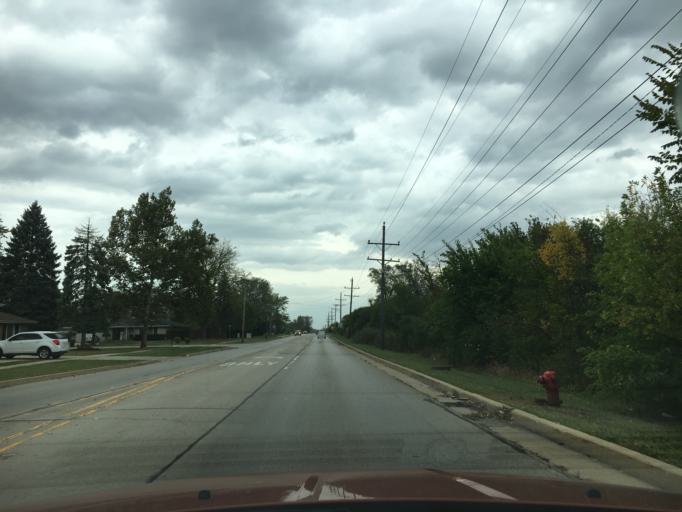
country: US
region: Illinois
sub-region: Cook County
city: Tinley Park
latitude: 41.6051
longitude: -87.7853
